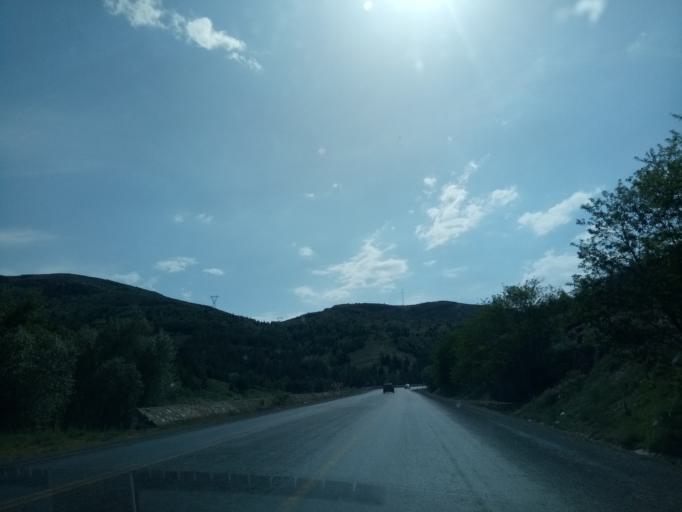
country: TR
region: Isparta
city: Bagkonak
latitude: 38.2480
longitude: 31.3571
